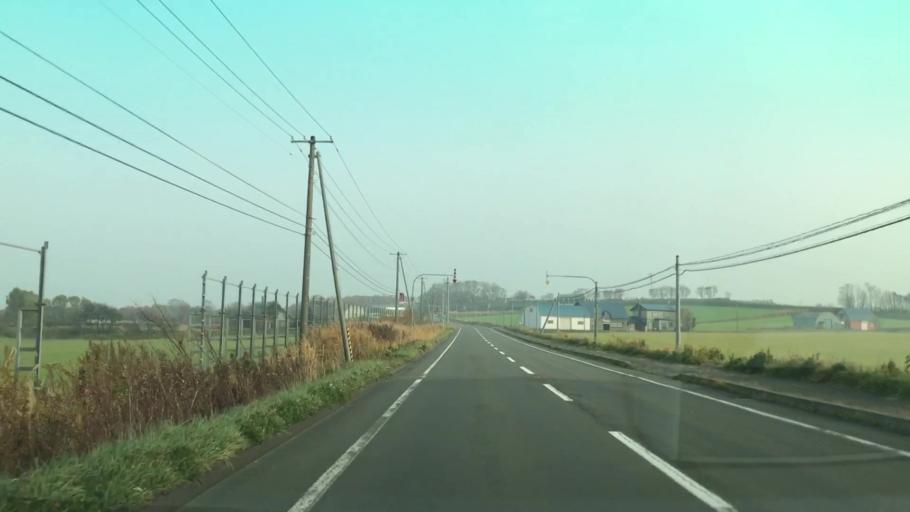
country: JP
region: Hokkaido
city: Ishikari
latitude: 43.2702
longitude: 141.4004
